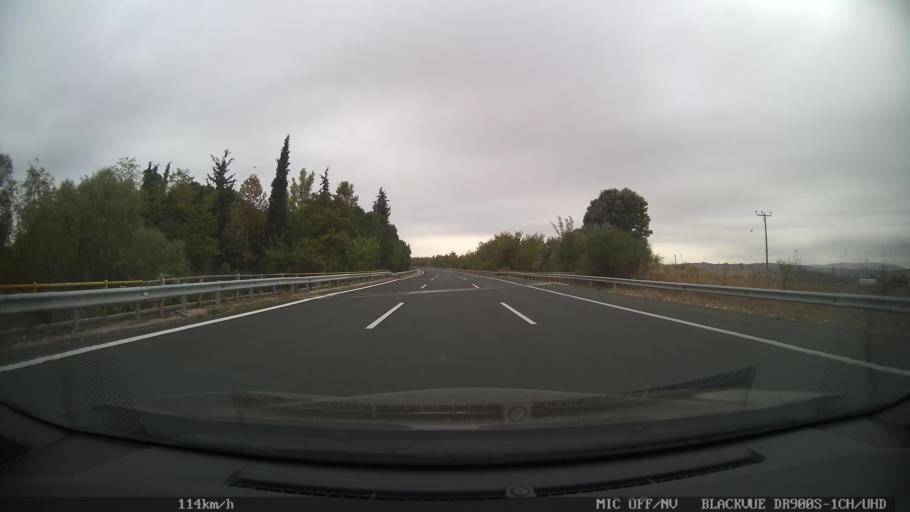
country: GR
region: Central Macedonia
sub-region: Nomos Pierias
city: Aiginio
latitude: 40.4982
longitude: 22.5649
